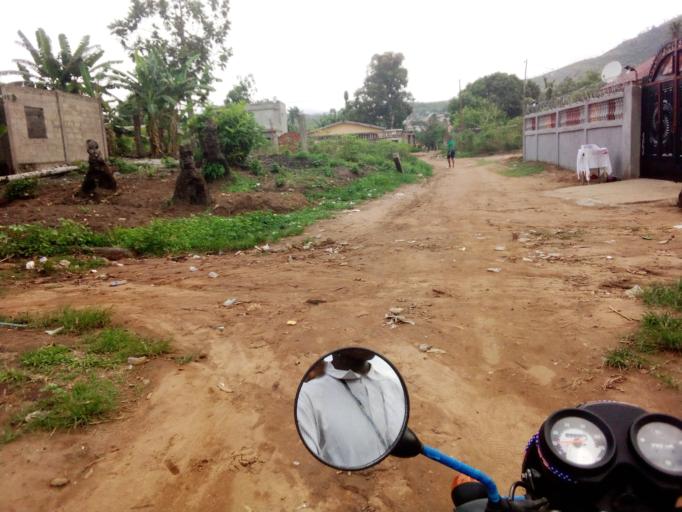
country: SL
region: Western Area
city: Waterloo
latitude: 8.3435
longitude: -13.0704
